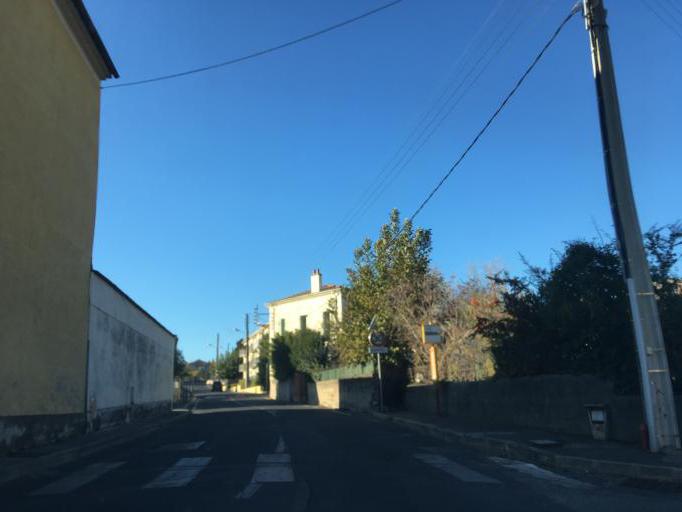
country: FR
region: Provence-Alpes-Cote d'Azur
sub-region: Departement du Var
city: Draguignan
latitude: 43.5428
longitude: 6.4588
